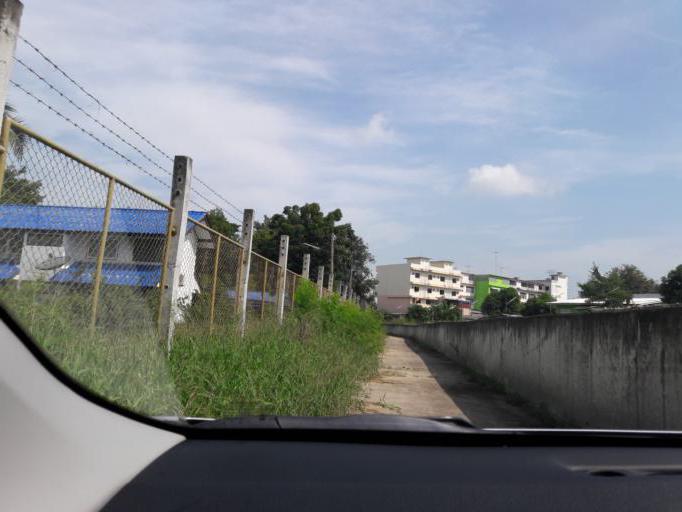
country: TH
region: Ang Thong
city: Ang Thong
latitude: 14.5923
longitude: 100.4481
